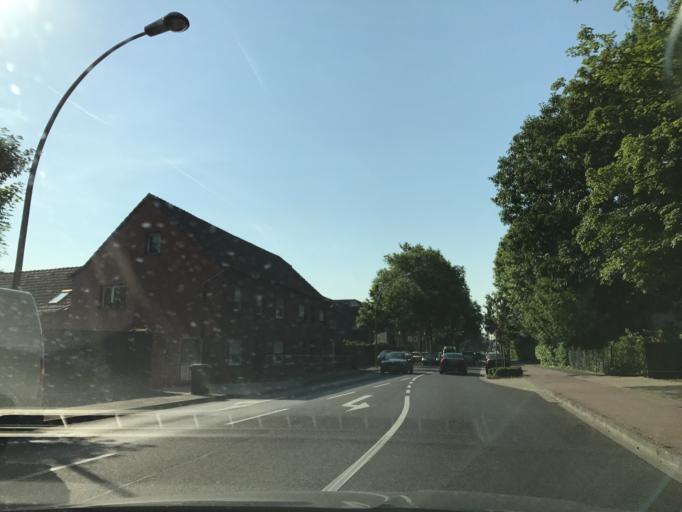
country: DE
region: North Rhine-Westphalia
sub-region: Regierungsbezirk Dusseldorf
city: Meerbusch
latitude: 51.2565
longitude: 6.6832
